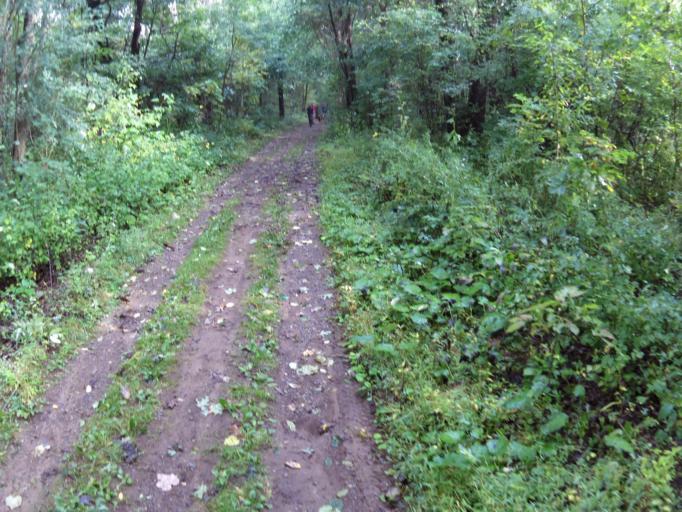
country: US
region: Virginia
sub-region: Rappahannock County
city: Washington
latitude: 38.7707
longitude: -78.2956
